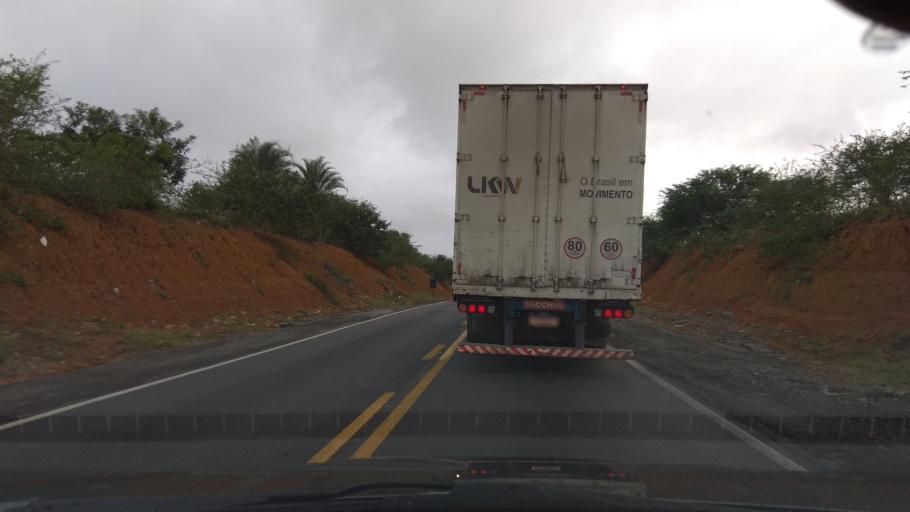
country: BR
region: Bahia
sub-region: Jaguaquara
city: Jaguaquara
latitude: -13.3812
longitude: -40.0208
